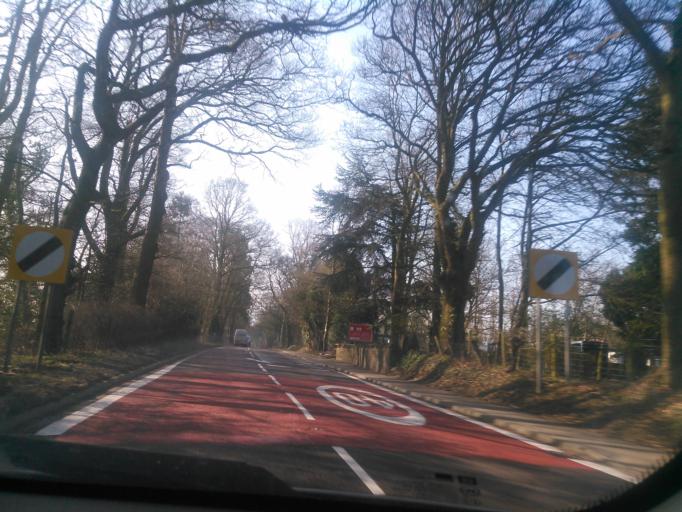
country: GB
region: England
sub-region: Shropshire
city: Craven Arms
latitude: 52.4552
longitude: -2.8372
